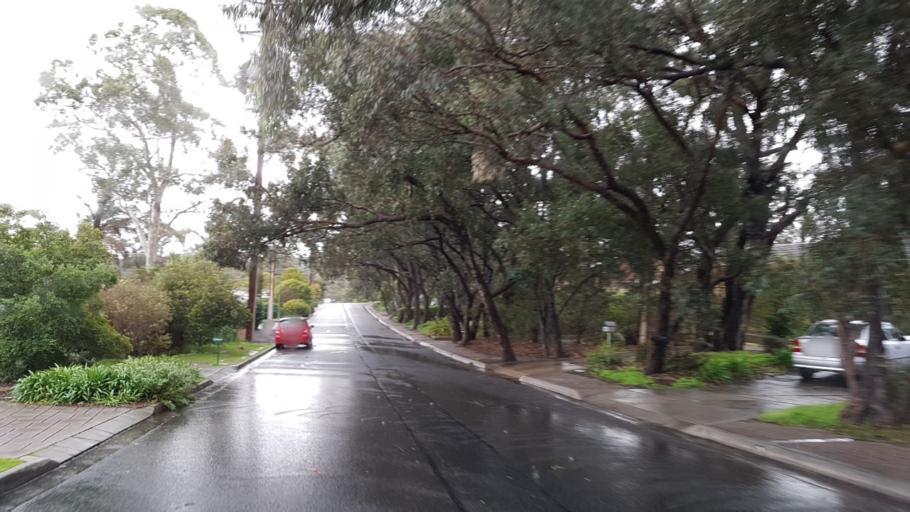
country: AU
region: South Australia
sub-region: Onkaparinga
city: Bedford Park
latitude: -35.0496
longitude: 138.5792
